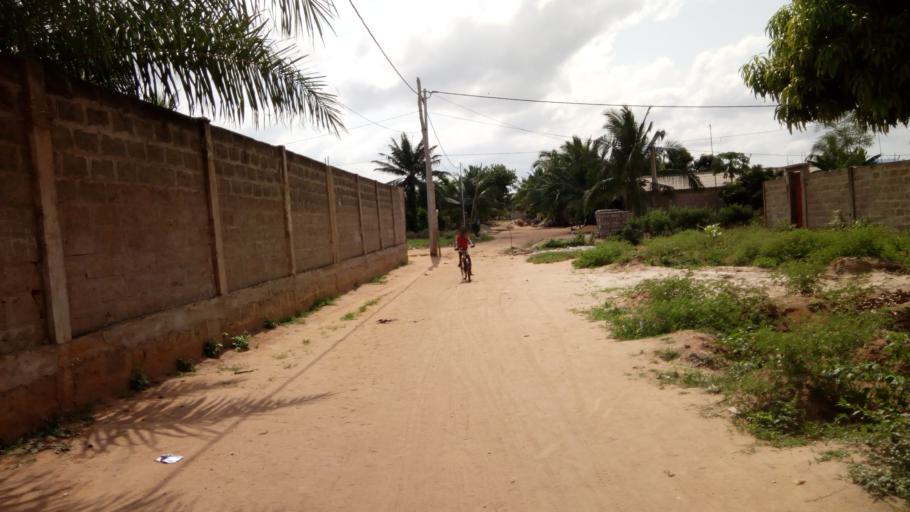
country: TG
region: Maritime
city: Lome
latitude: 6.2241
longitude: 1.1558
